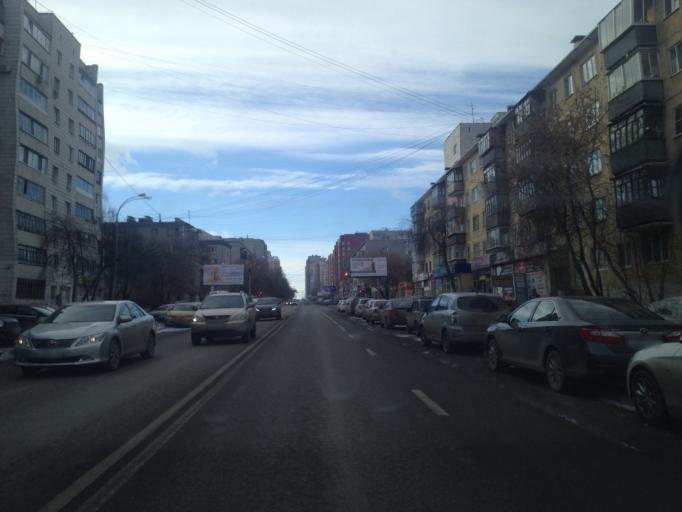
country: RU
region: Sverdlovsk
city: Yekaterinburg
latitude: 56.8138
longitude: 60.5994
